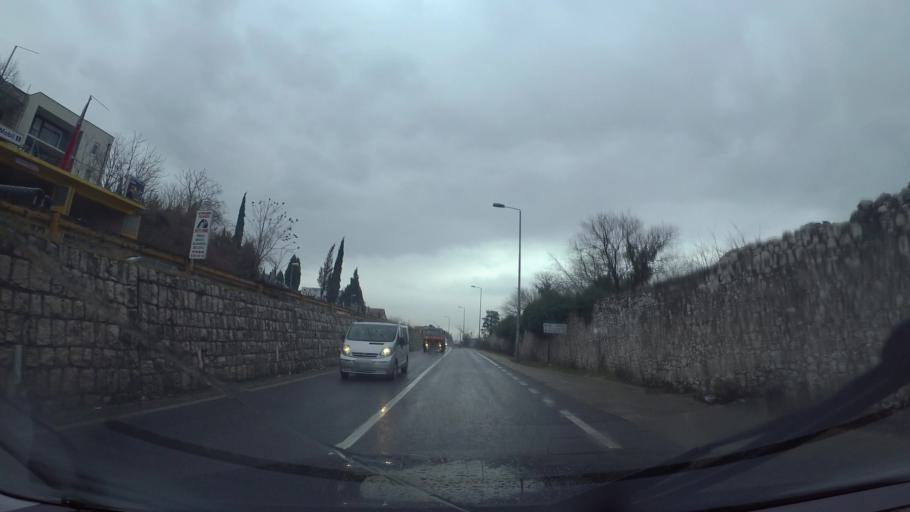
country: BA
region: Federation of Bosnia and Herzegovina
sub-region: Hercegovacko-Bosanski Kanton
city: Mostar
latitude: 43.3380
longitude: 17.8180
